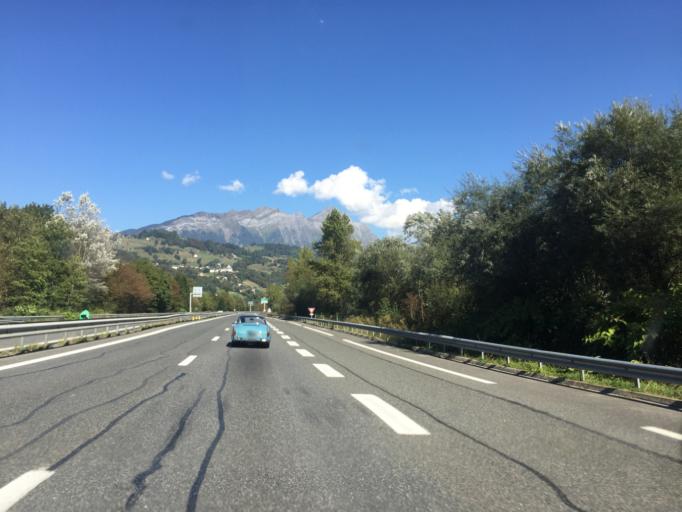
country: FR
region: Rhone-Alpes
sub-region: Departement de la Savoie
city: Marthod
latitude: 45.7066
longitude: 6.4061
